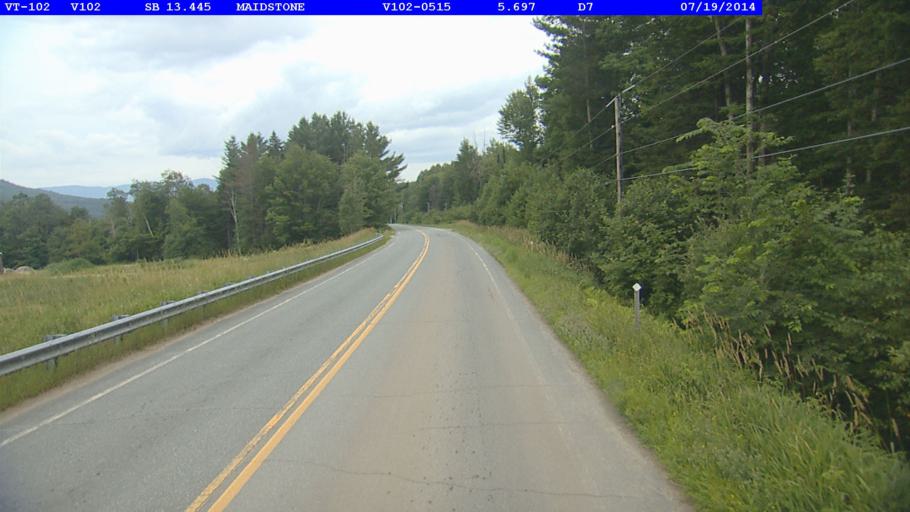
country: US
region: New Hampshire
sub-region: Coos County
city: Stratford
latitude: 44.6402
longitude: -71.5667
